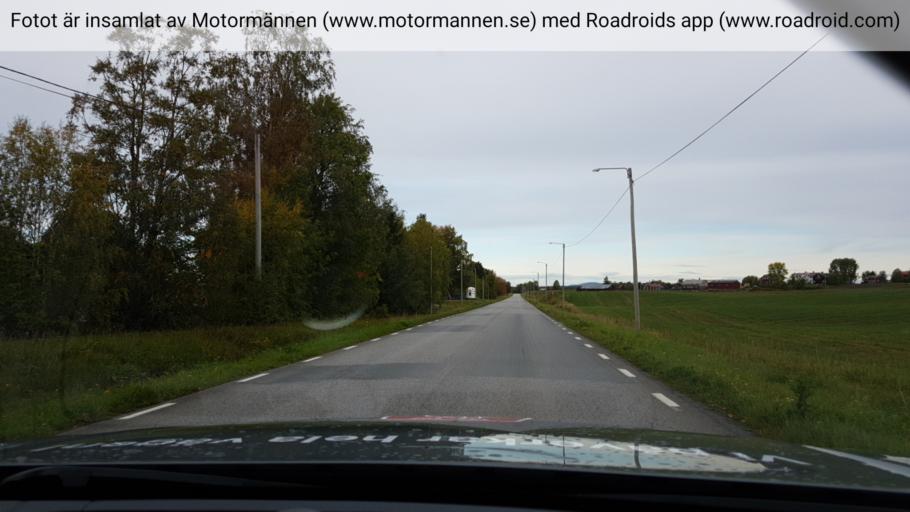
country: SE
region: Jaemtland
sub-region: Krokoms Kommun
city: Krokom
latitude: 63.2581
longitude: 14.4065
